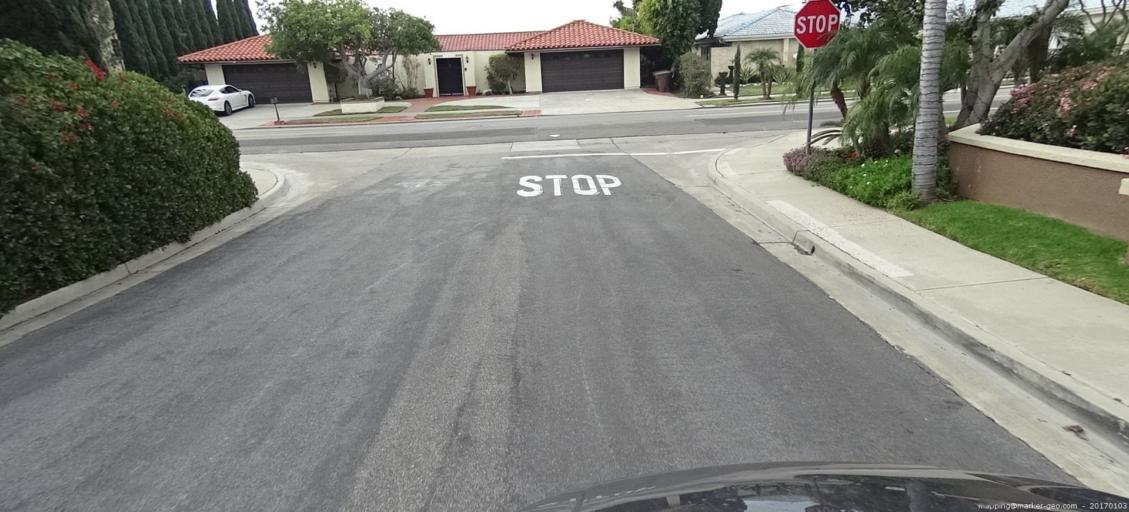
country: US
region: California
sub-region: Orange County
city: Dana Point
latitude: 33.4518
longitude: -117.6578
